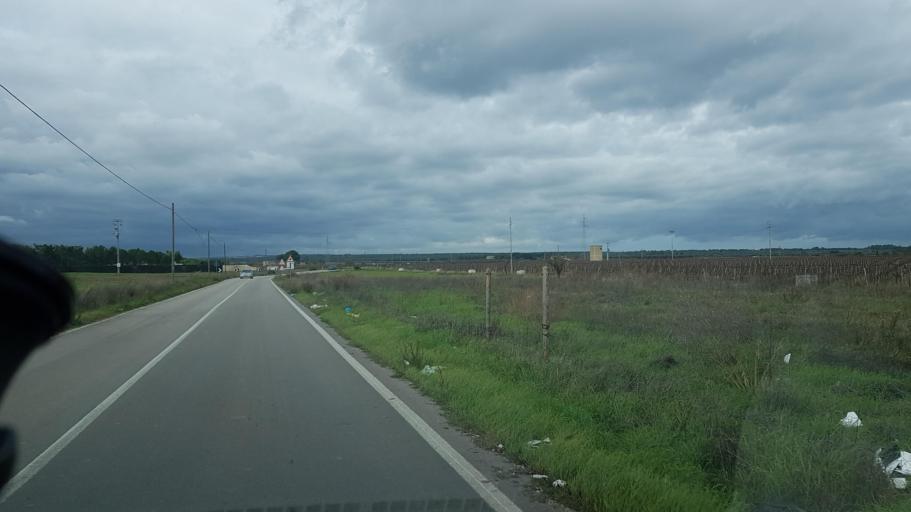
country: IT
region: Apulia
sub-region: Provincia di Brindisi
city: Francavilla Fontana
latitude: 40.5391
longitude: 17.5685
